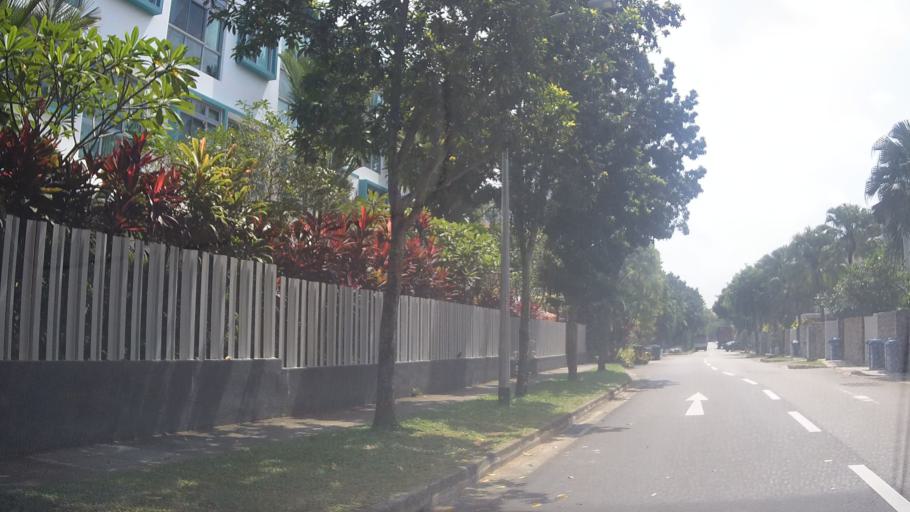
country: SG
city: Singapore
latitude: 1.3235
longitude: 103.7998
